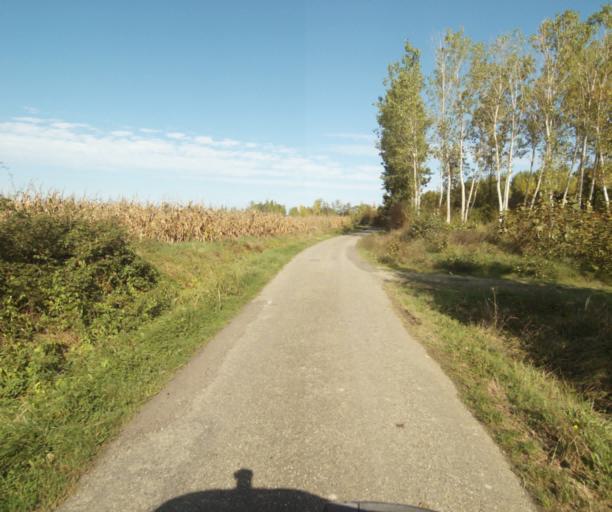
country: FR
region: Midi-Pyrenees
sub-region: Departement du Tarn-et-Garonne
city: Finhan
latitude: 43.9100
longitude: 1.2146
